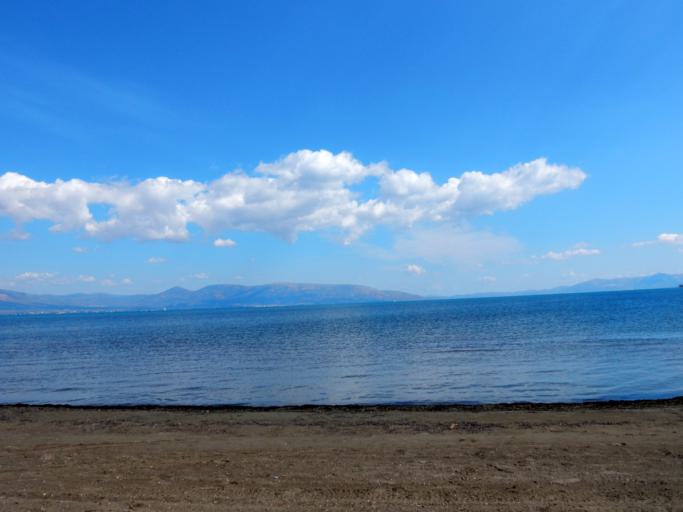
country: GR
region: Attica
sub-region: Nomarchia Anatolikis Attikis
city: Skala Oropou
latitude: 38.3272
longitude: 23.7800
